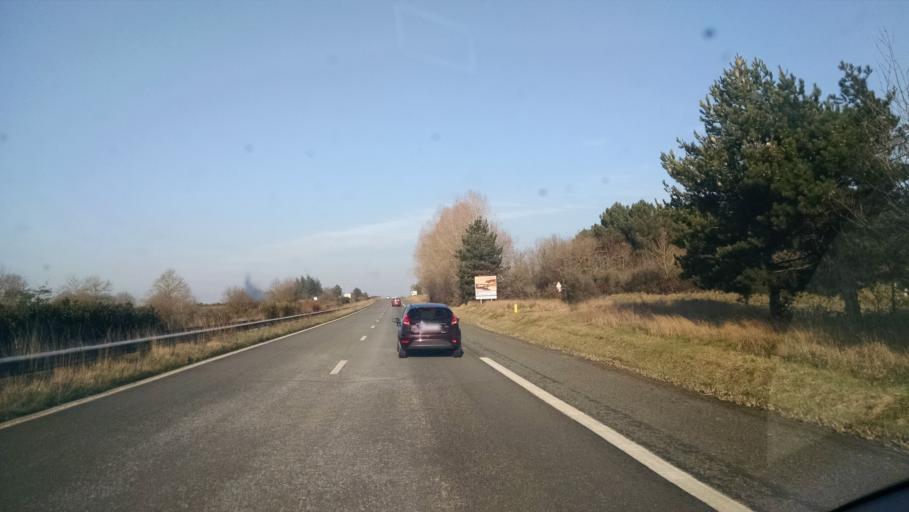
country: FR
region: Pays de la Loire
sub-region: Departement de la Loire-Atlantique
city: Missillac
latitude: 47.4634
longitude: -2.1522
